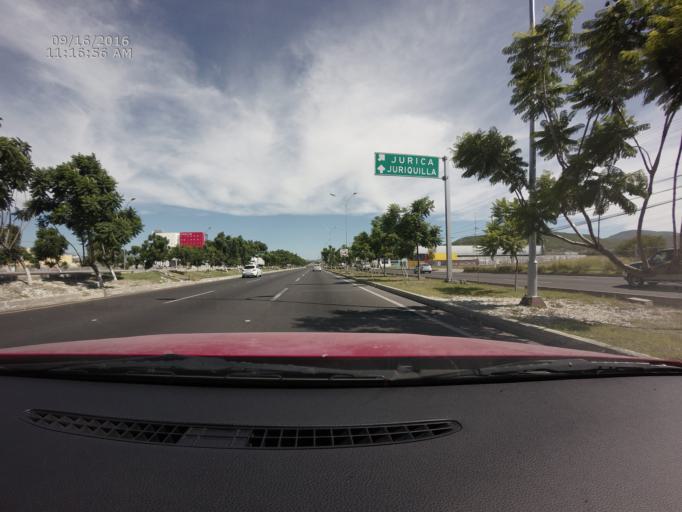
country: MX
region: Queretaro
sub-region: Queretaro
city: El Salitre
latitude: 20.6673
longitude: -100.4333
